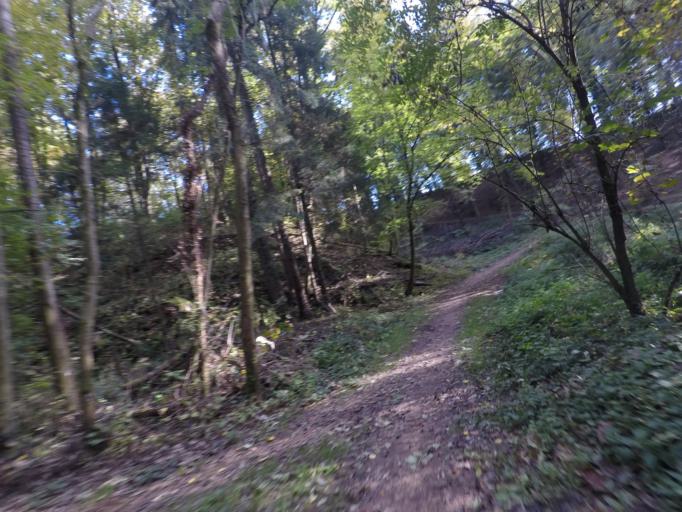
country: LU
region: Luxembourg
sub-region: Canton de Luxembourg
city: Hesperange
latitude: 49.5775
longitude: 6.1577
